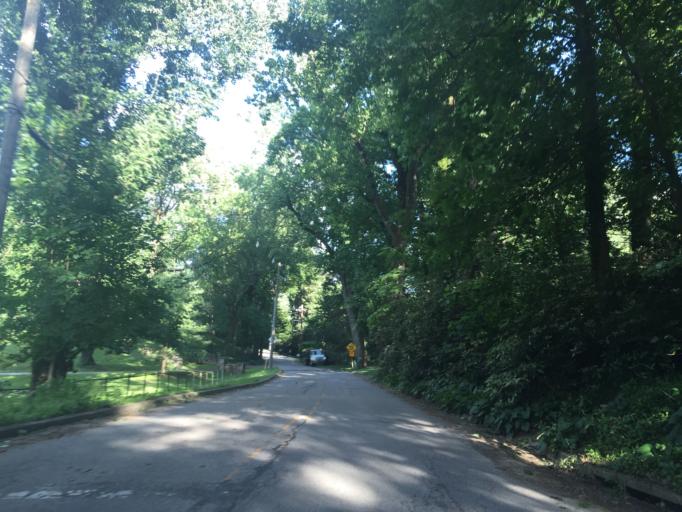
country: US
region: Maryland
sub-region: Baltimore County
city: Towson
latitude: 39.3692
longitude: -76.6409
